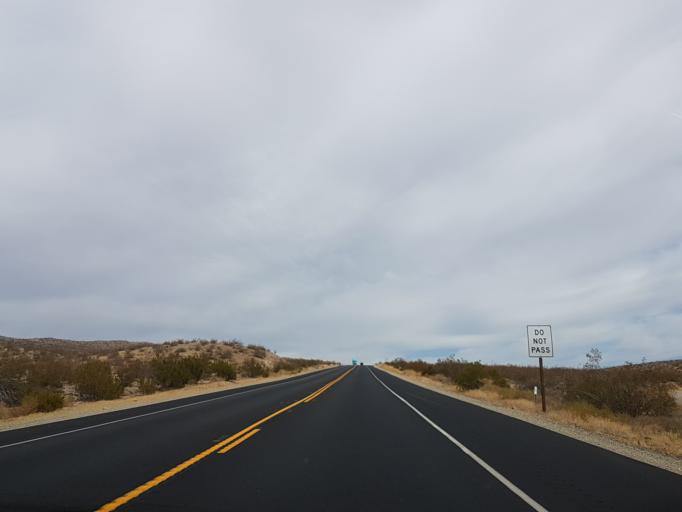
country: US
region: California
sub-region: Kern County
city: Ridgecrest
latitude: 35.4394
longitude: -117.6695
